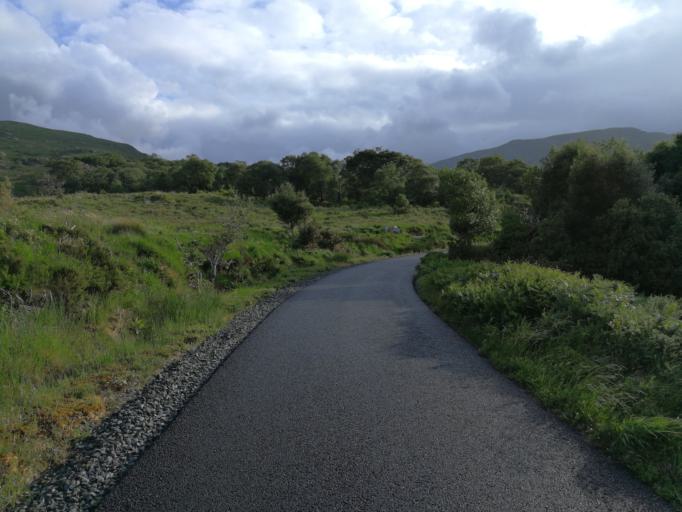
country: IE
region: Ulster
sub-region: County Donegal
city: Dunlewy
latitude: 55.0405
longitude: -7.9570
